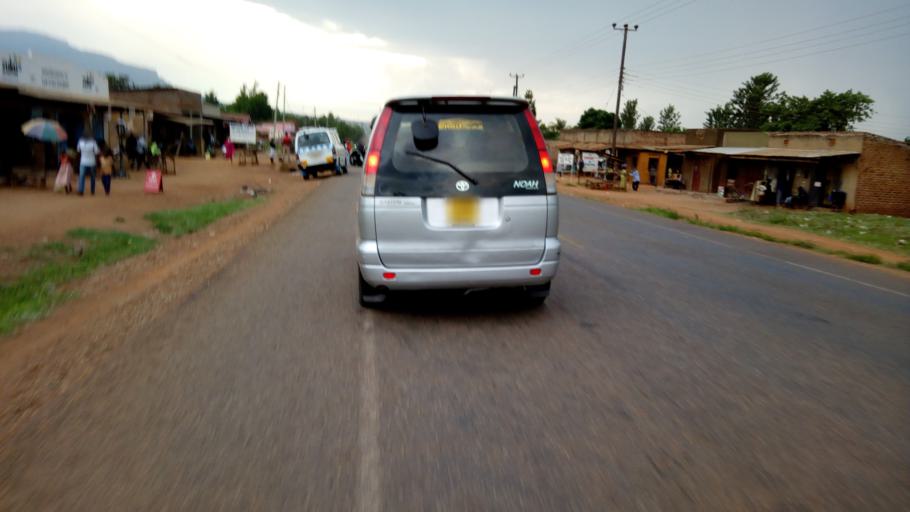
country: UG
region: Eastern Region
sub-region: Mbale District
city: Mbale
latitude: 1.1223
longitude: 34.1691
